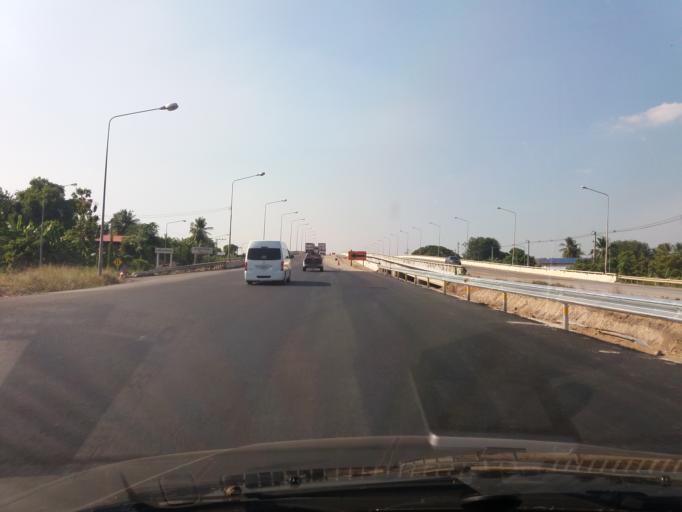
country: TH
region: Nakhon Sawan
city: Nakhon Sawan
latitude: 15.6313
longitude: 100.1034
